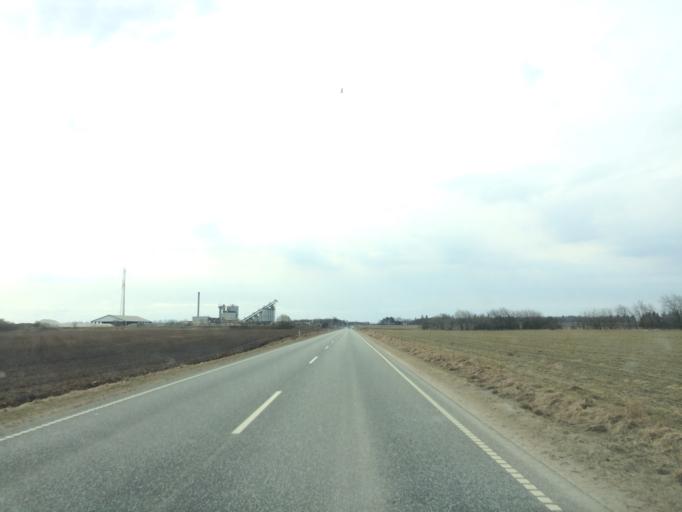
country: DK
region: Central Jutland
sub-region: Ringkobing-Skjern Kommune
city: Videbaek
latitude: 56.0959
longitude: 8.5076
